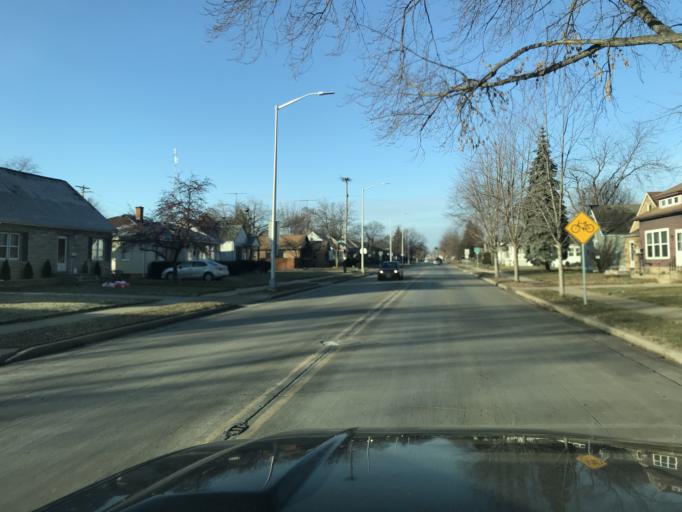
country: US
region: Wisconsin
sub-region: Kenosha County
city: Kenosha
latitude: 42.5661
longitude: -87.8485
